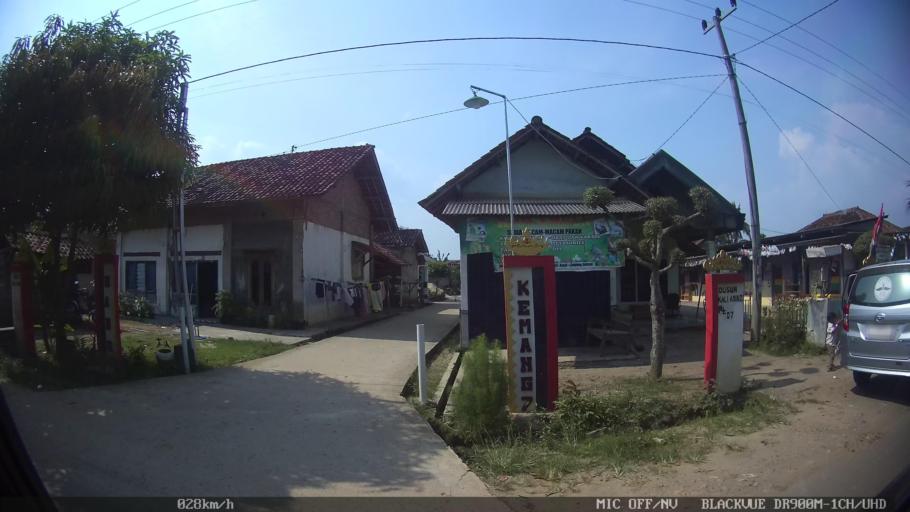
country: ID
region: Lampung
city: Natar
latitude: -5.3069
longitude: 105.2207
